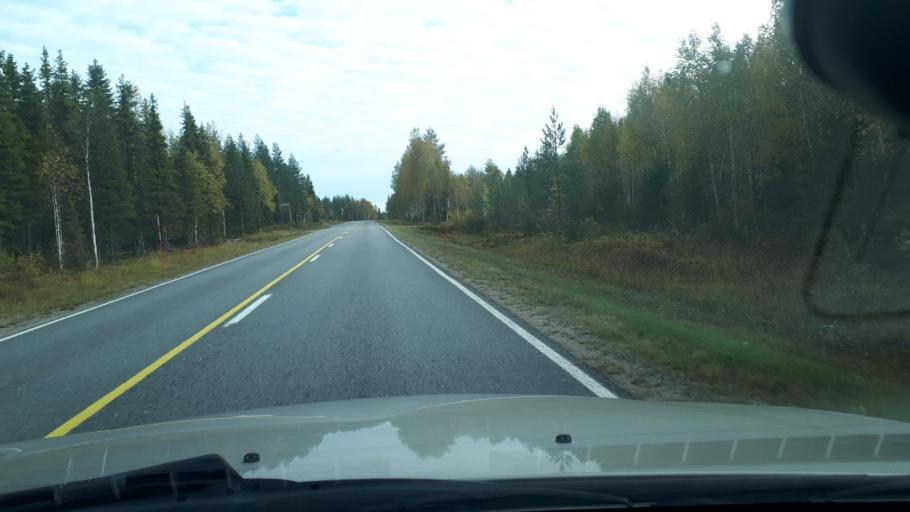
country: FI
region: Lapland
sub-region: Rovaniemi
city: Ranua
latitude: 65.9626
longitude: 25.9557
